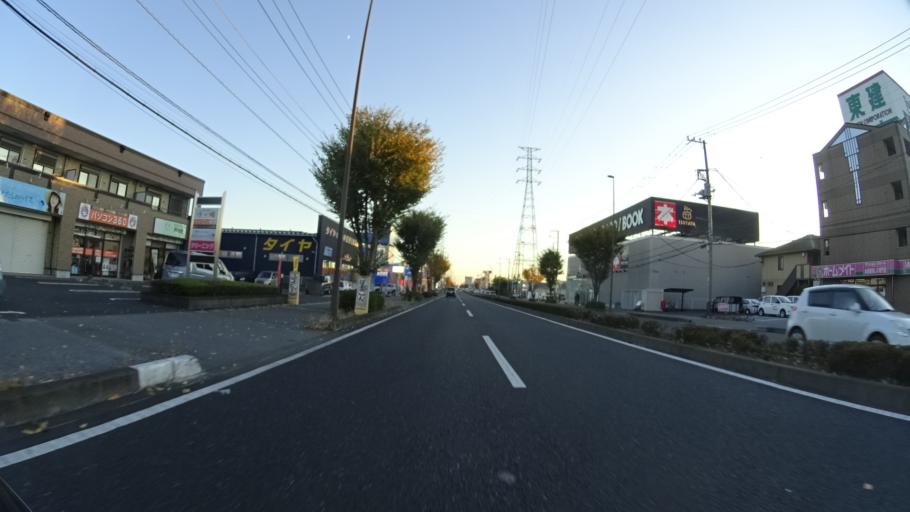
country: JP
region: Tochigi
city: Kaminokawa
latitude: 36.5008
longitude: 139.9050
